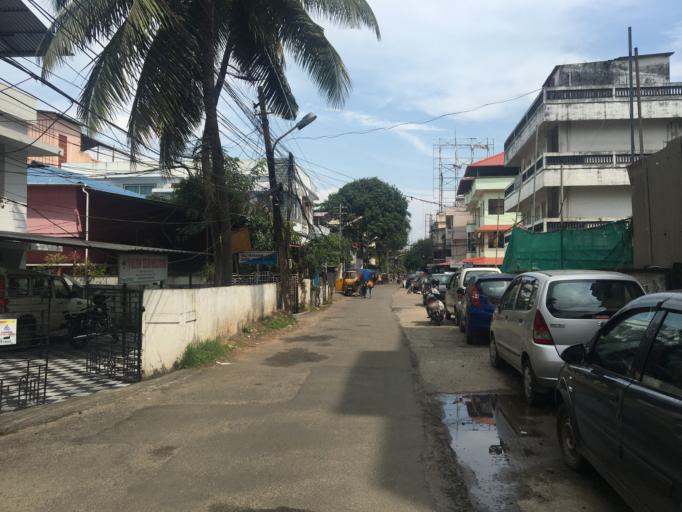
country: IN
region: Kerala
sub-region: Ernakulam
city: Cochin
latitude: 9.9760
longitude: 76.2873
